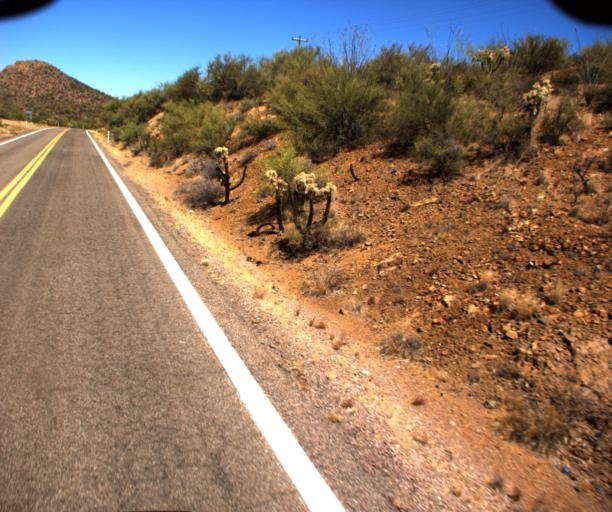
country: US
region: Arizona
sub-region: Pima County
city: Sells
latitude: 32.1701
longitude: -112.1456
